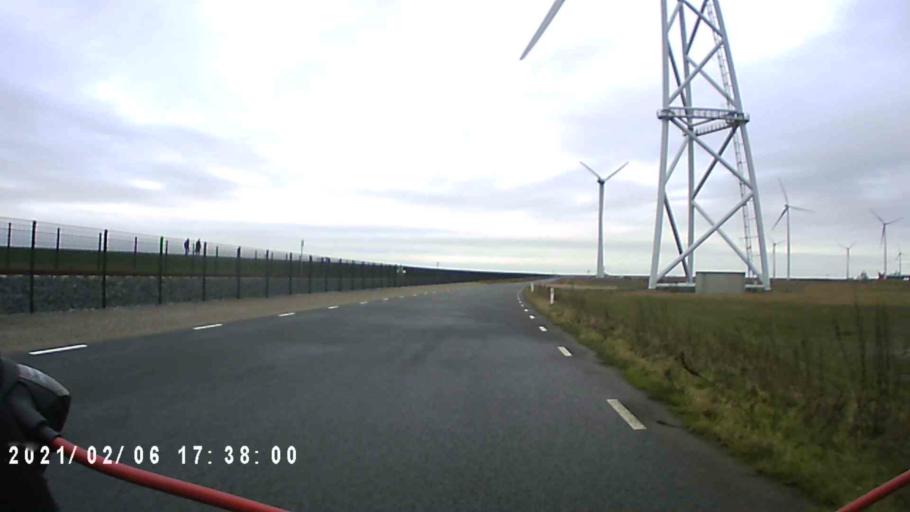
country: NL
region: Groningen
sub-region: Gemeente Appingedam
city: Appingedam
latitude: 53.4547
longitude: 6.7995
